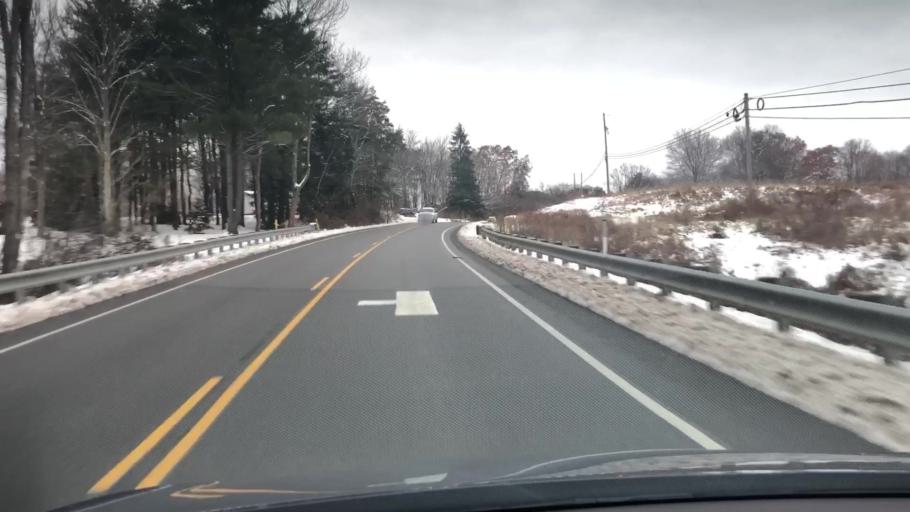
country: US
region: Pennsylvania
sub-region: Clearfield County
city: Treasure Lake
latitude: 41.1766
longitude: -78.6485
